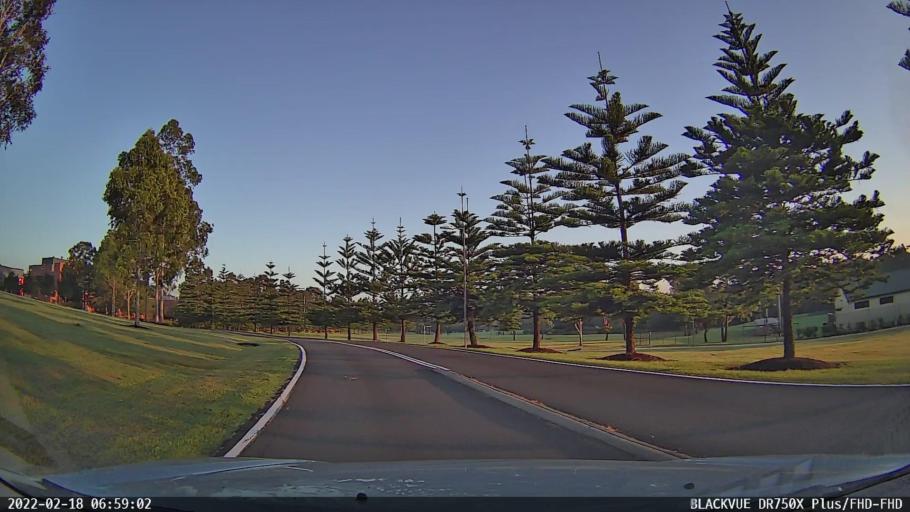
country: AU
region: New South Wales
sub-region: Penrith Municipality
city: Kingswood Park
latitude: -33.7699
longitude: 150.7308
